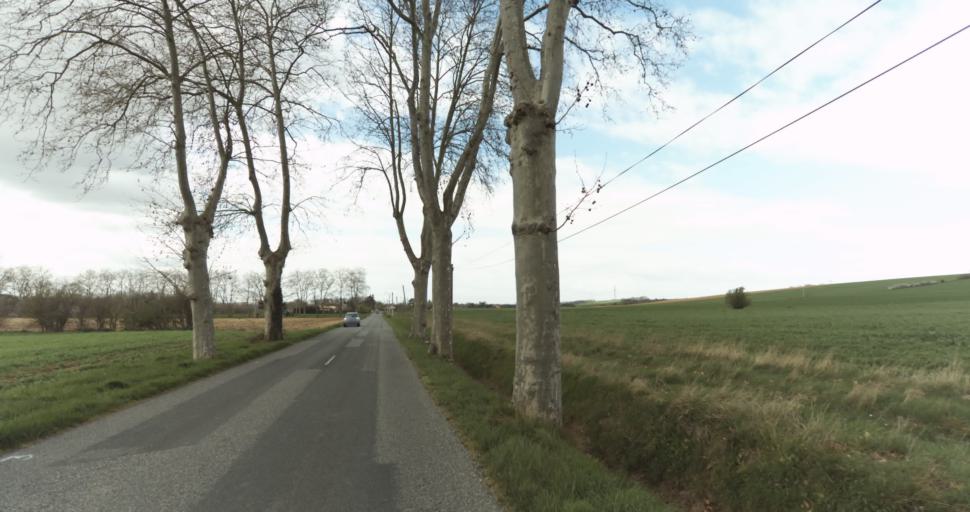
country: FR
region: Midi-Pyrenees
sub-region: Departement de la Haute-Garonne
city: Auterive
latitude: 43.3736
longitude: 1.4667
